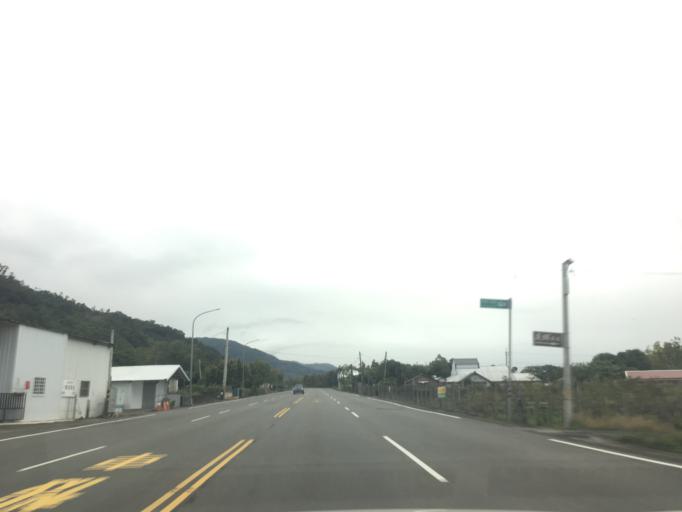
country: TW
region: Taiwan
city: Taitung City
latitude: 22.7328
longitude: 121.0563
